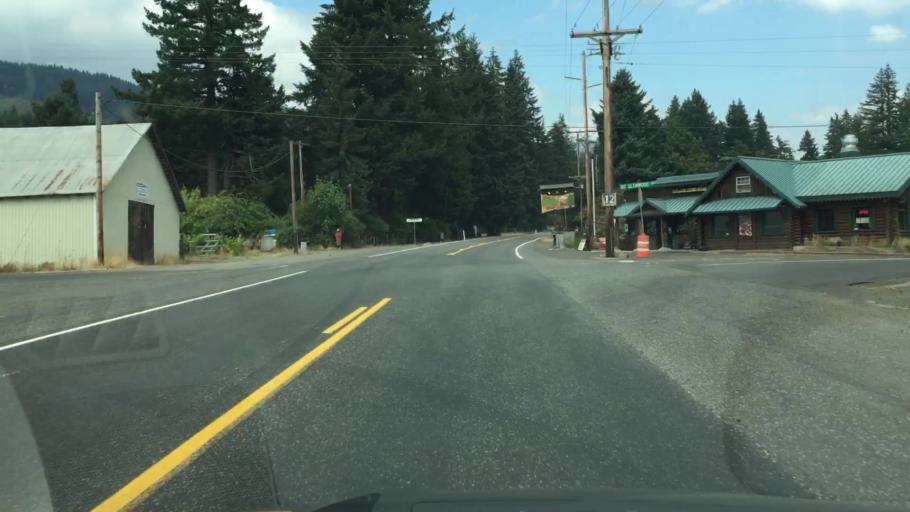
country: US
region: Washington
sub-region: Klickitat County
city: White Salmon
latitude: 45.8496
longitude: -121.5093
